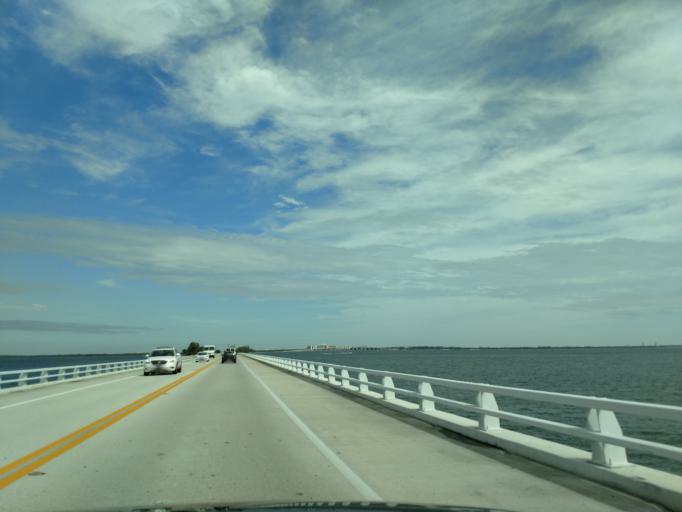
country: US
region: Florida
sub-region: Lee County
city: Sanibel
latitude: 26.4602
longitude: -82.0338
